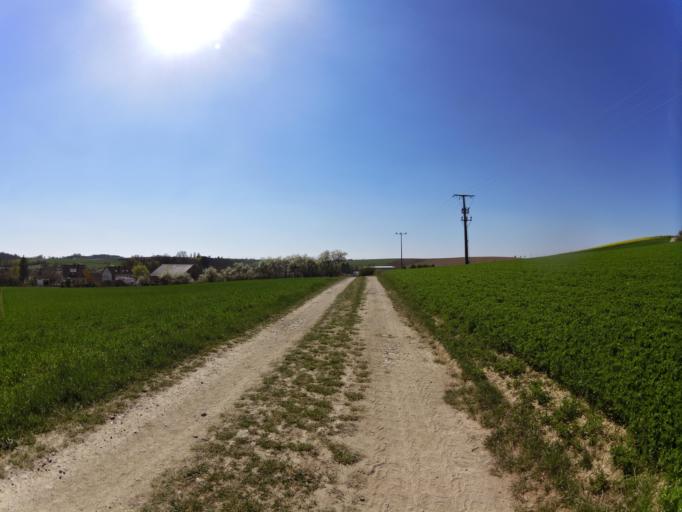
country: DE
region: Bavaria
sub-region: Regierungsbezirk Unterfranken
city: Winterhausen
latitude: 49.6764
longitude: 9.9979
